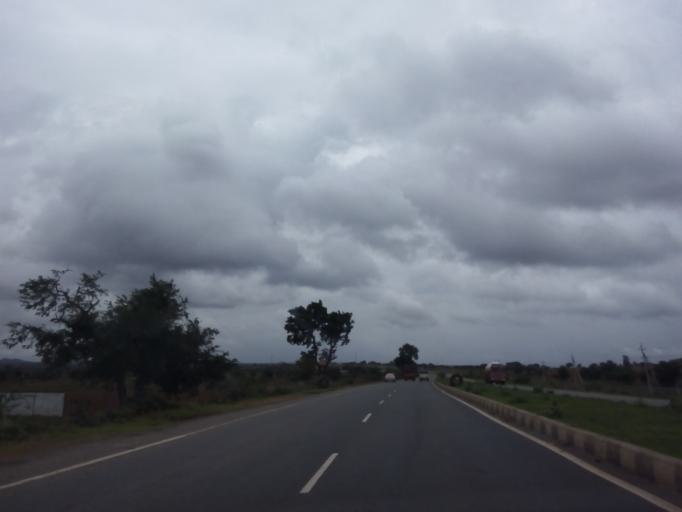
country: IN
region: Karnataka
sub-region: Haveri
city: Haveri
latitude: 14.7701
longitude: 75.4247
